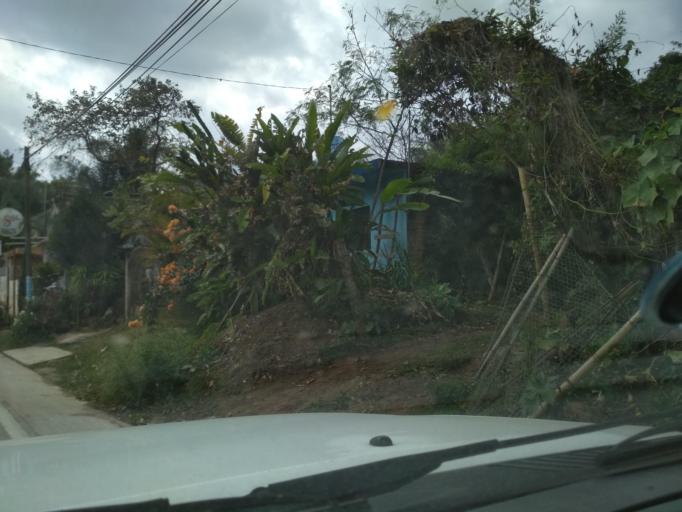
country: MX
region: Veracruz
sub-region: Coatepec
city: Bella Esperanza
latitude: 19.4562
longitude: -96.8615
